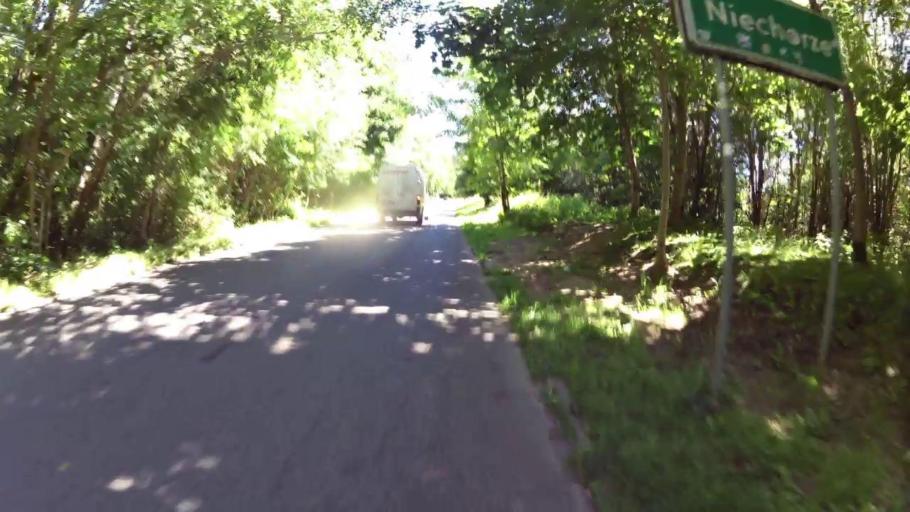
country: PL
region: West Pomeranian Voivodeship
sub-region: Powiat gryficki
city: Rewal
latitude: 54.0893
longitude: 15.0426
